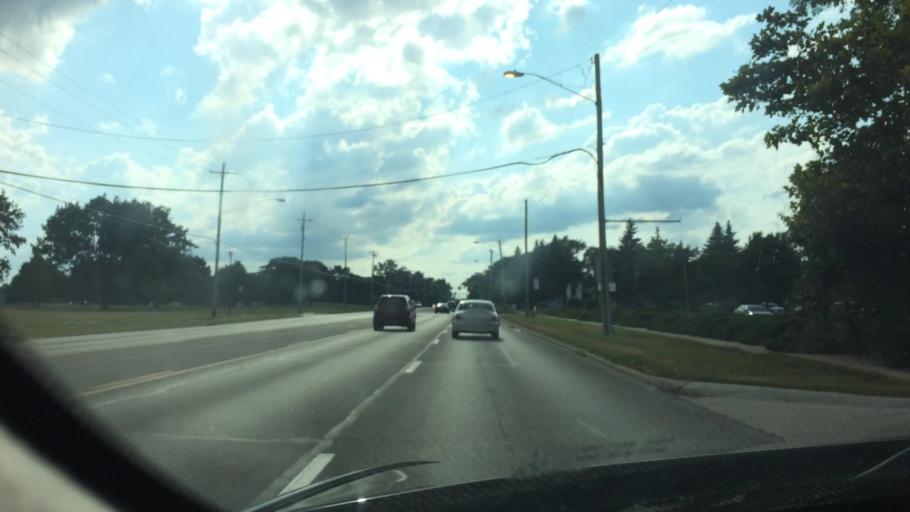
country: US
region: Ohio
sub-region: Lucas County
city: Maumee
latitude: 41.5945
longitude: -83.6502
